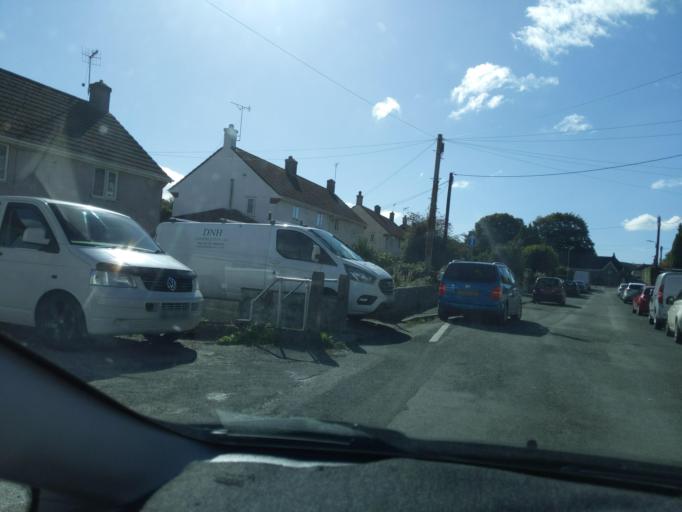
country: GB
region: England
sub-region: Plymouth
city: Plymstock
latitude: 50.3567
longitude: -4.0715
